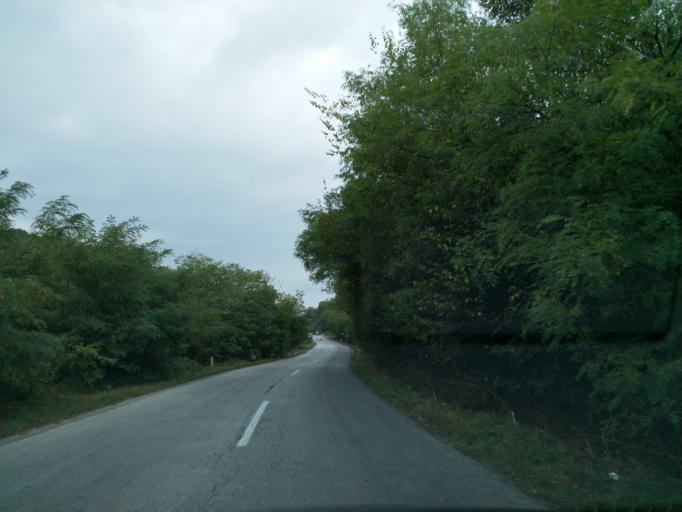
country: RS
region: Central Serbia
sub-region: Pomoravski Okrug
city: Jagodina
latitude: 44.0362
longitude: 21.1897
